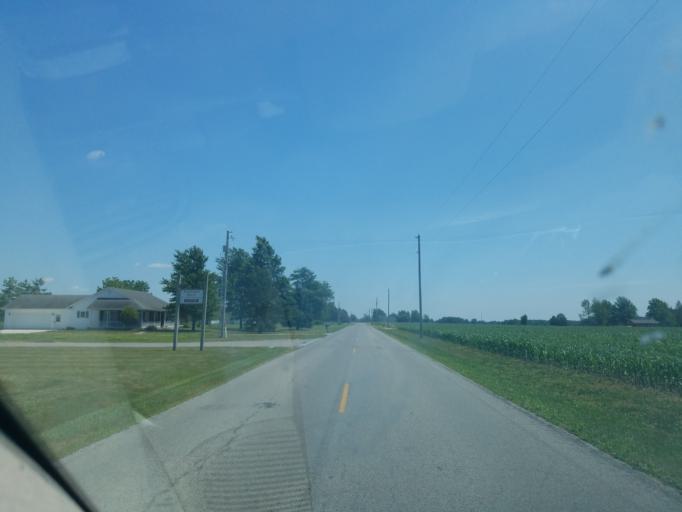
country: US
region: Ohio
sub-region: Allen County
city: Elida
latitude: 40.7872
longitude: -84.2628
